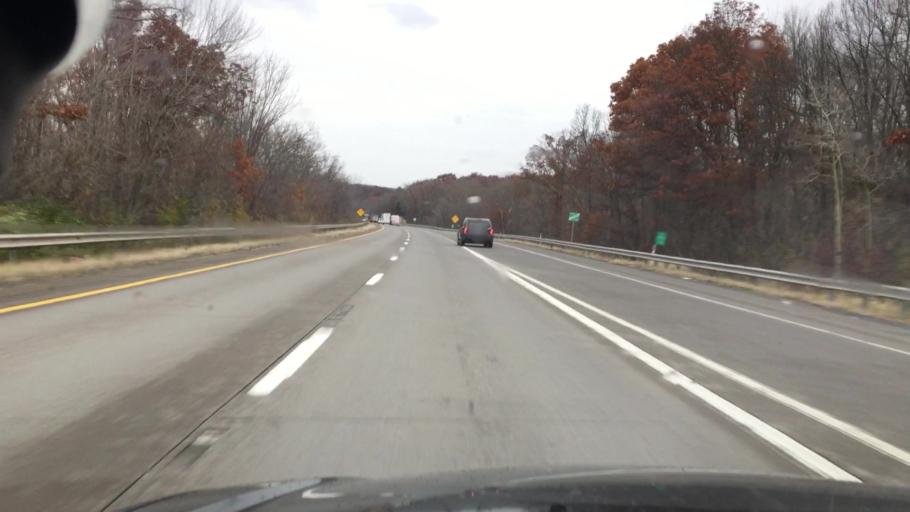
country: US
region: Pennsylvania
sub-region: Luzerne County
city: Mountain Top
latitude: 41.1057
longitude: -75.9606
